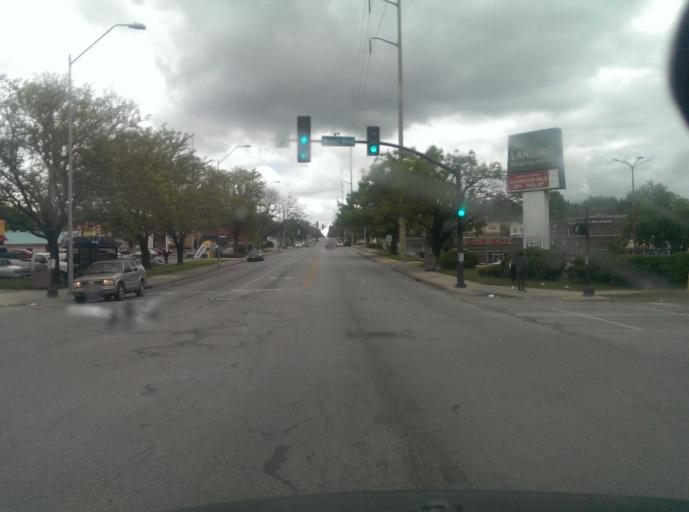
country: US
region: Kansas
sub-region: Johnson County
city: Mission Hills
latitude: 39.0113
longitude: -94.5747
